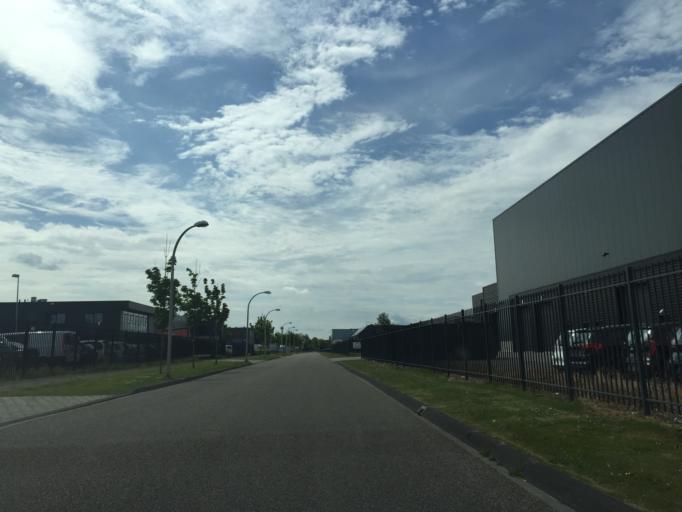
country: NL
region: South Holland
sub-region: Gemeente Pijnacker-Nootdorp
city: Pijnacker
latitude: 51.9969
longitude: 4.4003
